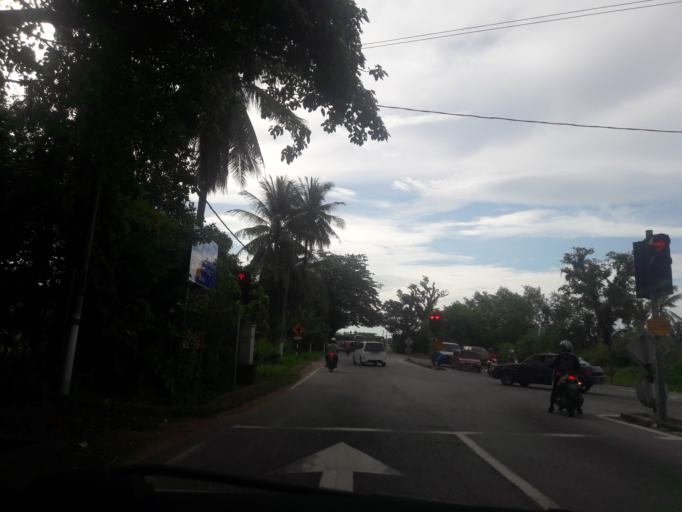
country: MY
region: Kedah
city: Sungai Petani
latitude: 5.6326
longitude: 100.5183
